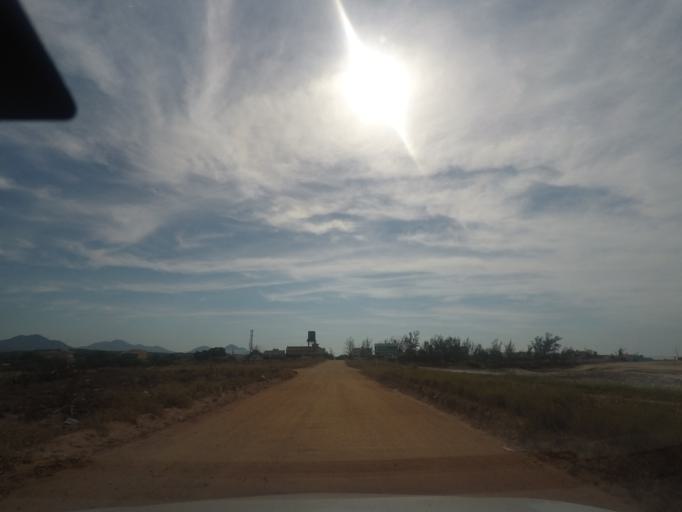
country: BR
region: Rio de Janeiro
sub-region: Marica
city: Marica
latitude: -22.9594
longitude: -42.8301
